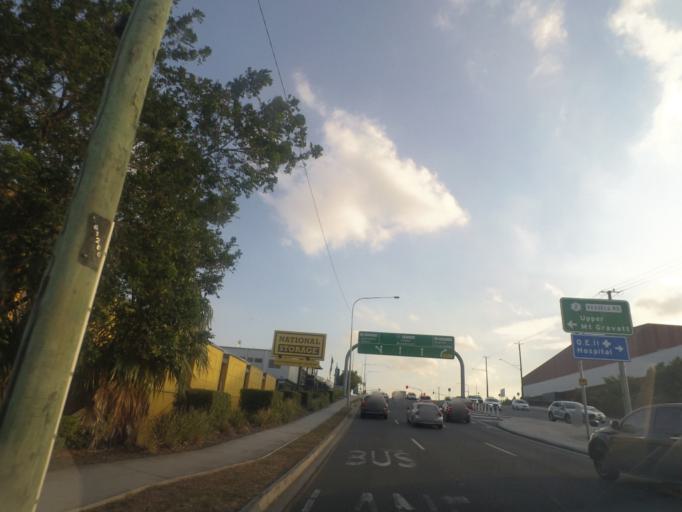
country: AU
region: Queensland
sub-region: Brisbane
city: Nathan
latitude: -27.5591
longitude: 153.0666
